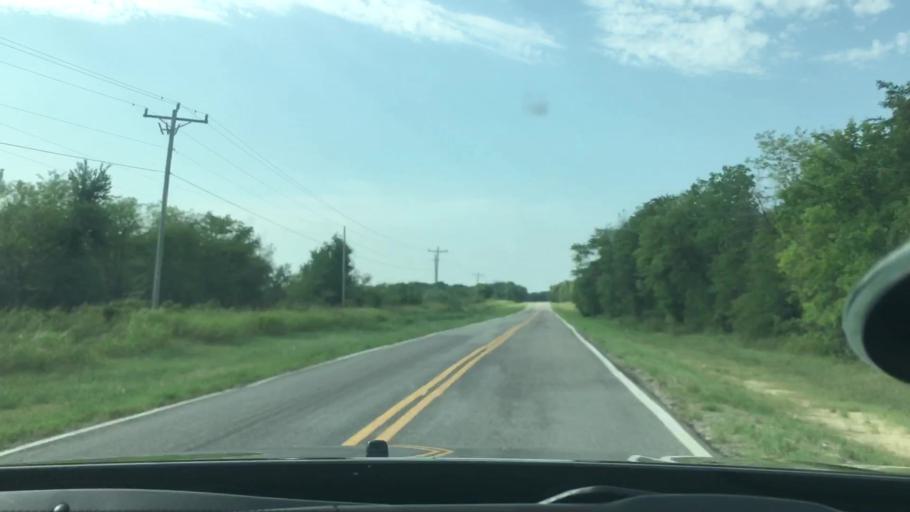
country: US
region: Oklahoma
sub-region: Johnston County
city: Tishomingo
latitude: 34.1784
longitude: -96.5839
